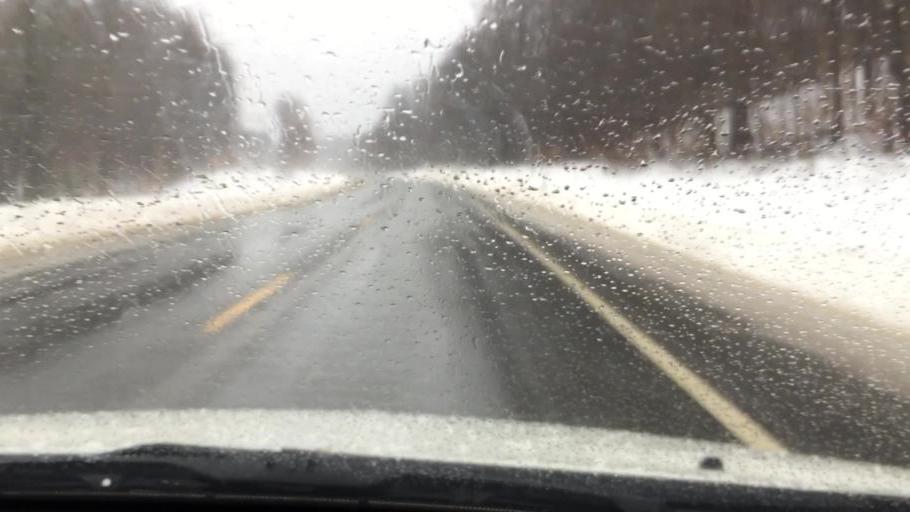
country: US
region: Michigan
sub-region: Antrim County
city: Mancelona
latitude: 45.0148
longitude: -85.0648
